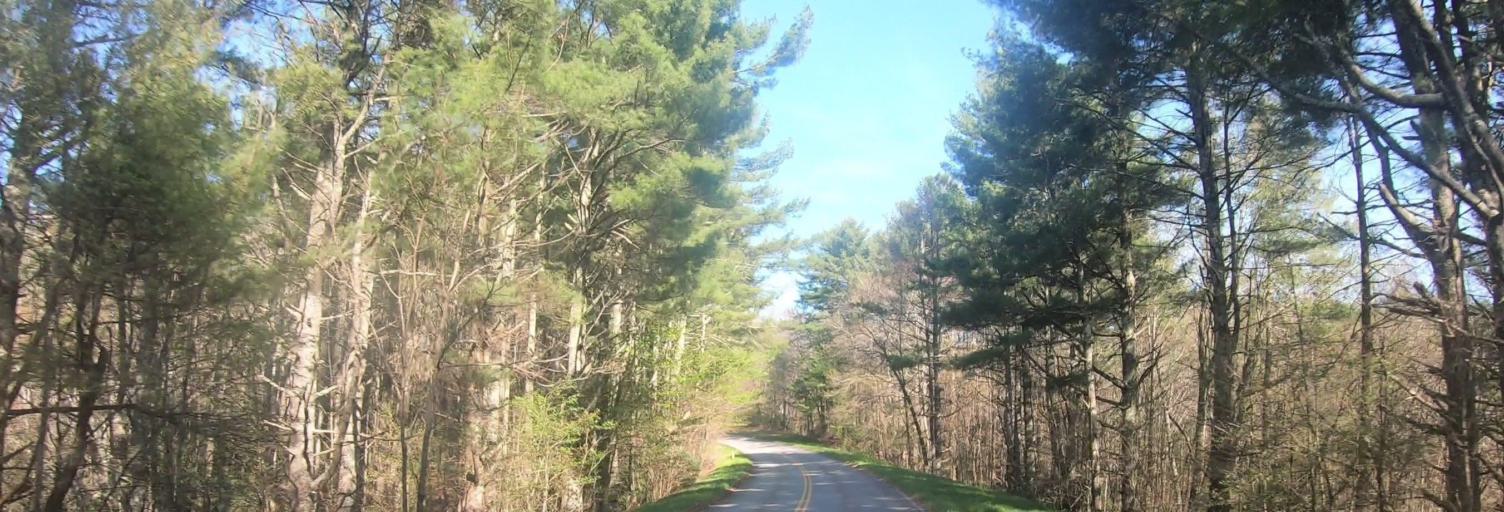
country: US
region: North Carolina
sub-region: Watauga County
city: Boone
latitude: 36.2299
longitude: -81.5449
